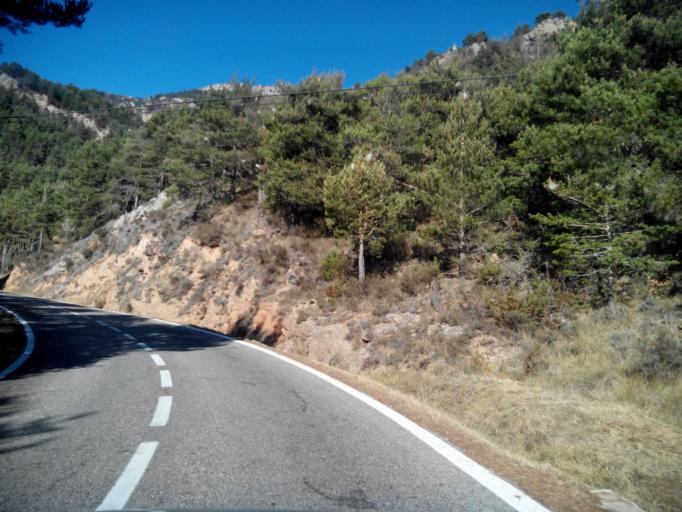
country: ES
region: Catalonia
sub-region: Provincia de Barcelona
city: Capolat
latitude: 42.0907
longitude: 1.7809
